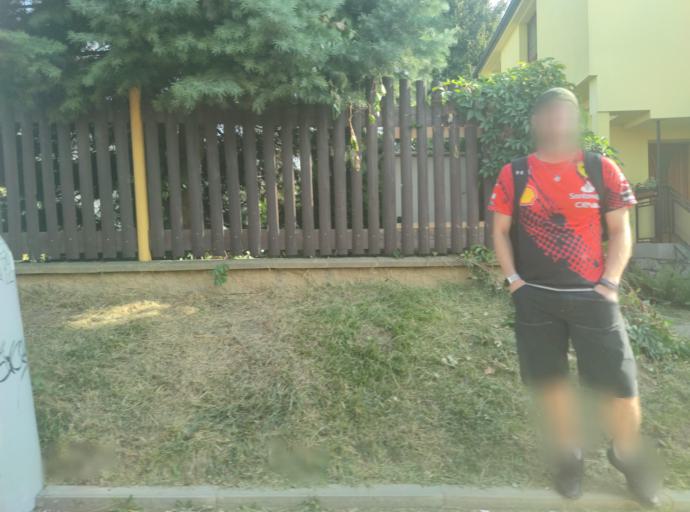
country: CZ
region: South Moravian
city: Podoli
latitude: 49.1774
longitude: 16.6908
